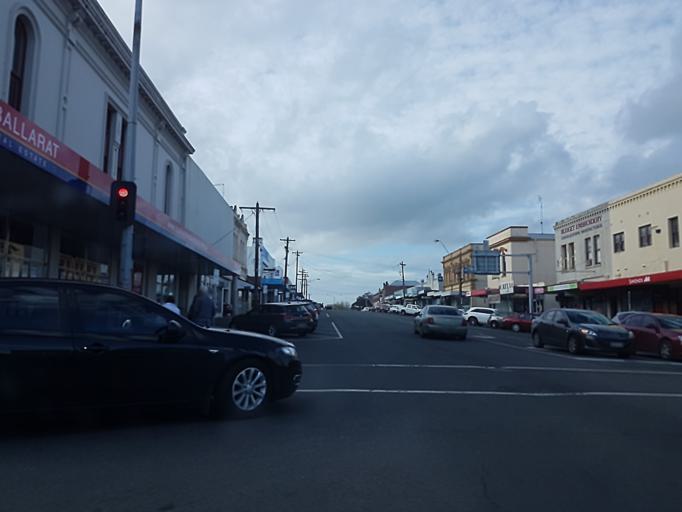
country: AU
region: Victoria
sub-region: Ballarat North
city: Ballarat Central
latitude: -37.5622
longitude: 143.8558
